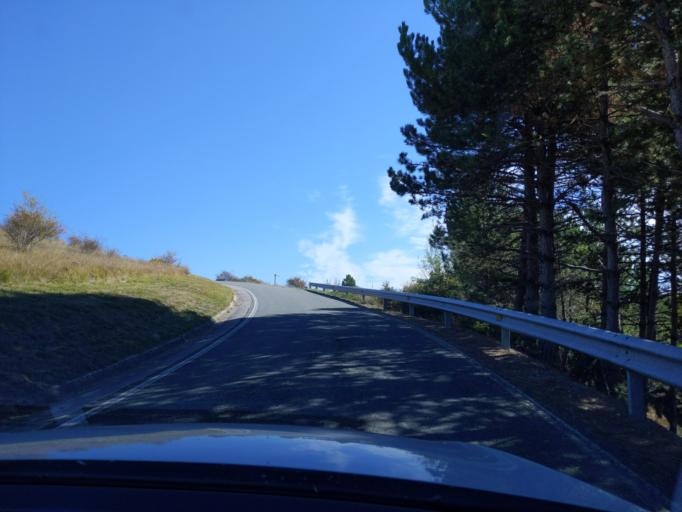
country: ES
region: Navarre
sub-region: Provincia de Navarra
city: Egues-Uharte
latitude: 42.8368
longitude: -1.5664
